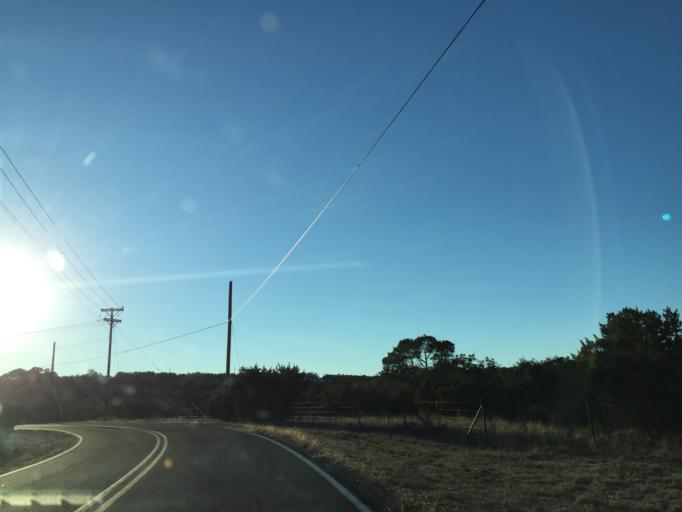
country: US
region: Texas
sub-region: Travis County
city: Lago Vista
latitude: 30.5024
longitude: -98.0565
